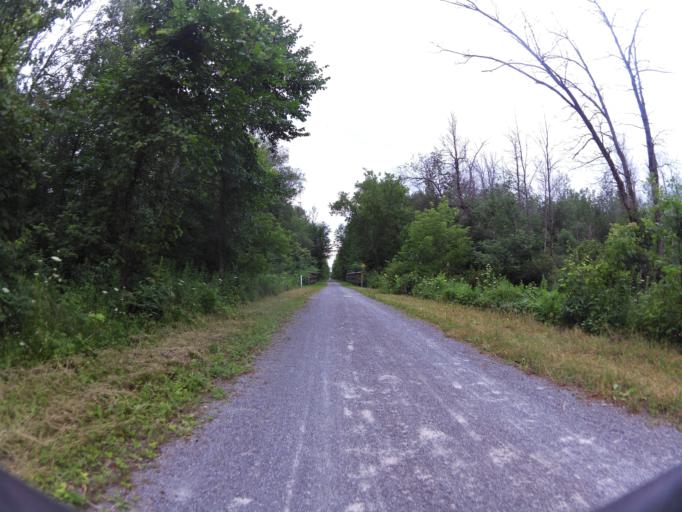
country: CA
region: Ontario
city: Ottawa
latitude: 45.2421
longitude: -75.6200
